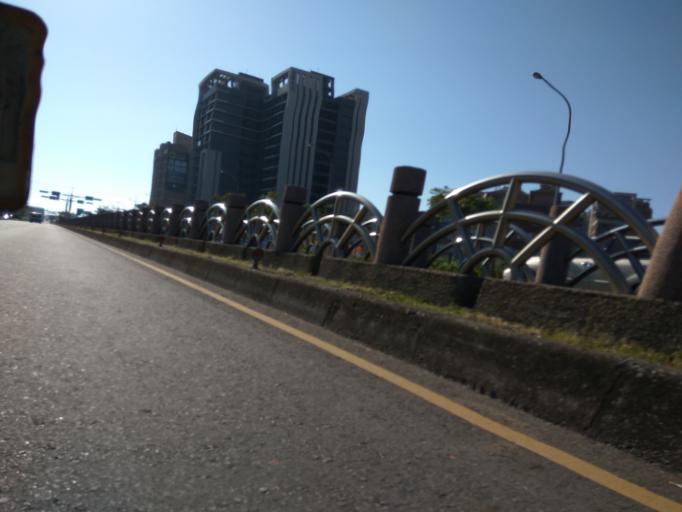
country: TW
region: Taiwan
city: Taoyuan City
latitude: 25.0063
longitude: 121.2160
